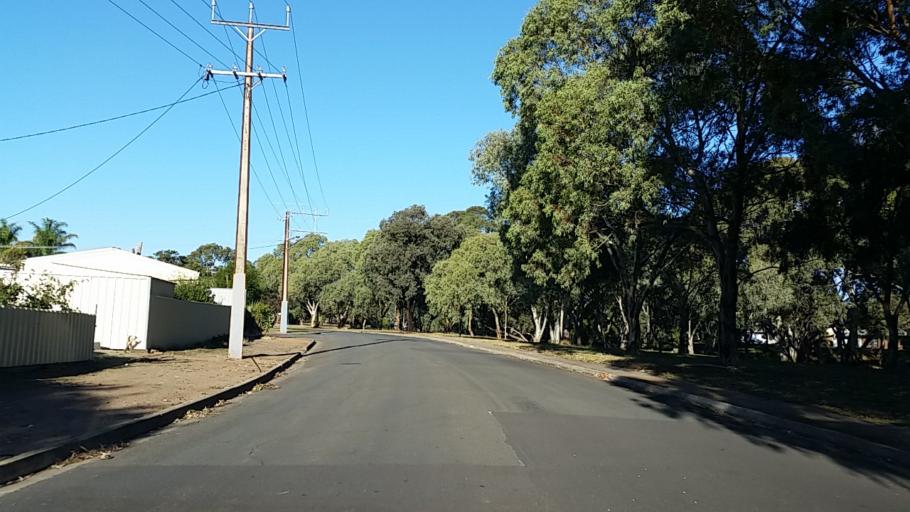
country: AU
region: South Australia
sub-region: Onkaparinga
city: Morphett Vale
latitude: -35.1215
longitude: 138.5344
